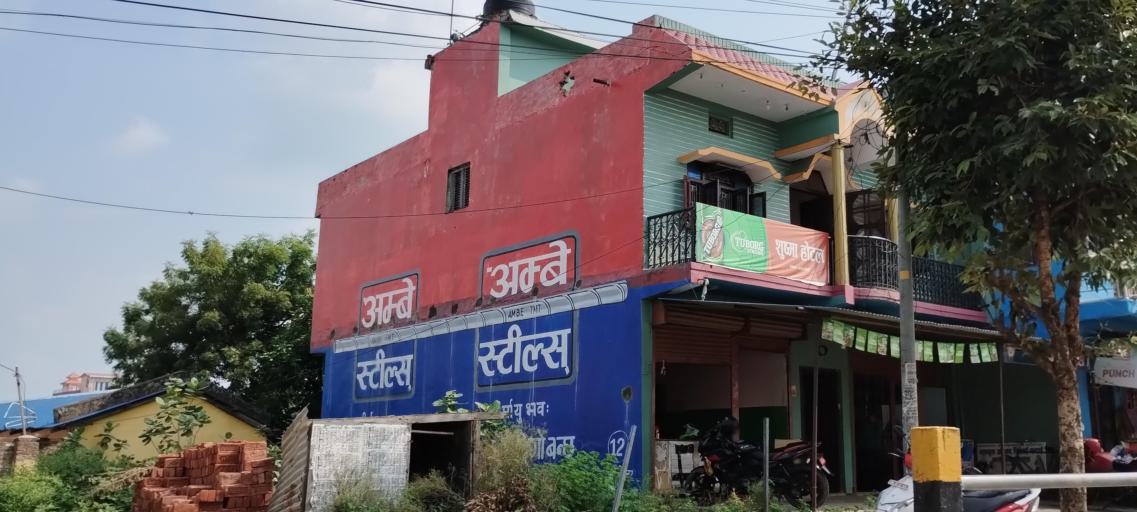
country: NP
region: Mid Western
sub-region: Bheri Zone
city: Nepalgunj
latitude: 28.0980
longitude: 81.6645
